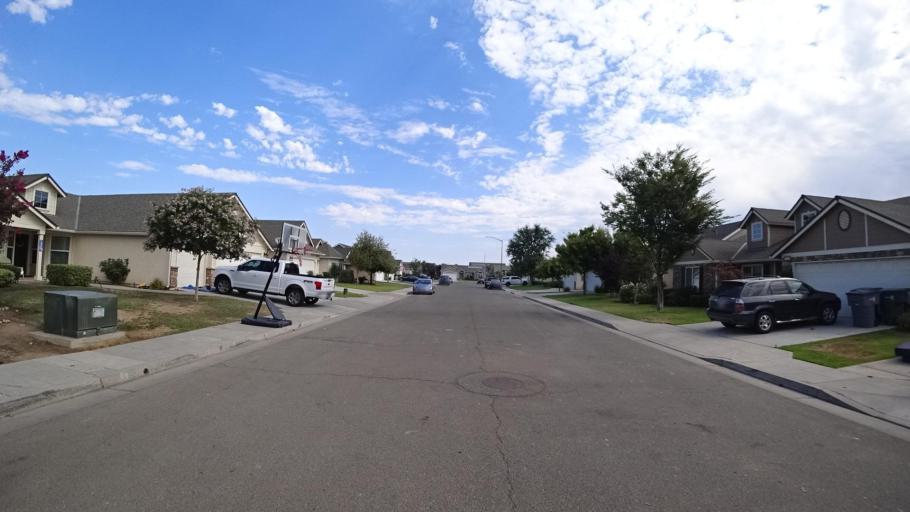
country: US
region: California
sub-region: Fresno County
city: Tarpey Village
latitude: 36.7810
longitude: -119.6708
